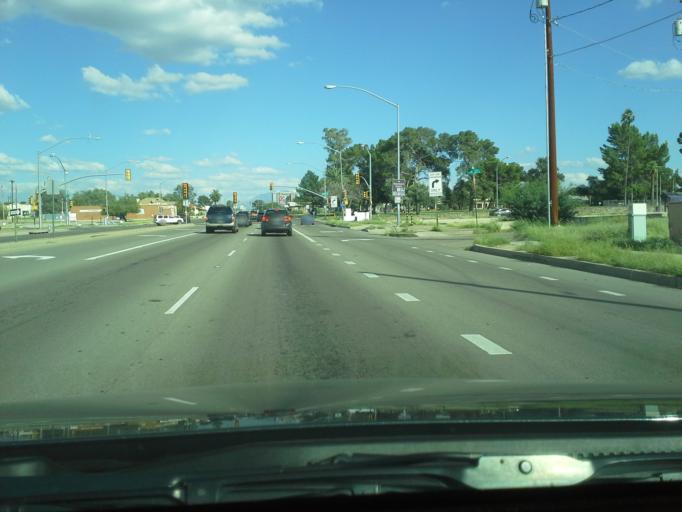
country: US
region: Arizona
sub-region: Pima County
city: South Tucson
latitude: 32.2359
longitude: -110.9729
